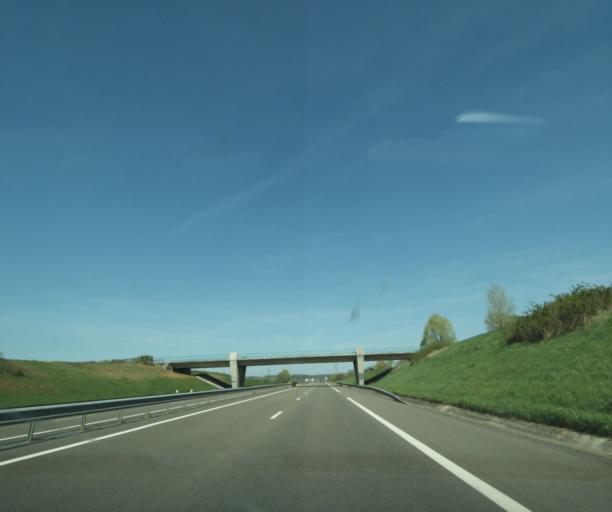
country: FR
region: Bourgogne
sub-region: Departement de la Nievre
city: Coulanges-les-Nevers
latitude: 46.9930
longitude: 3.2060
